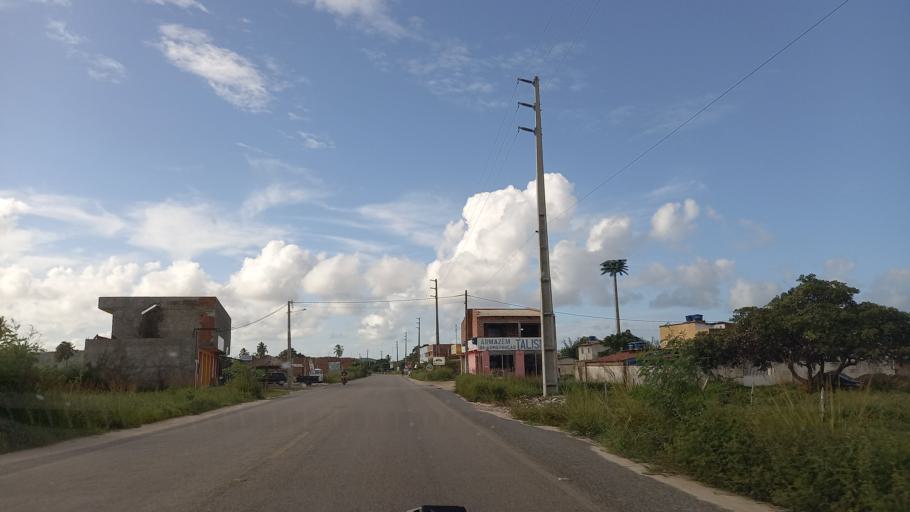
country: BR
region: Pernambuco
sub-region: Tamandare
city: Tamandare
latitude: -8.7329
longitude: -35.0959
